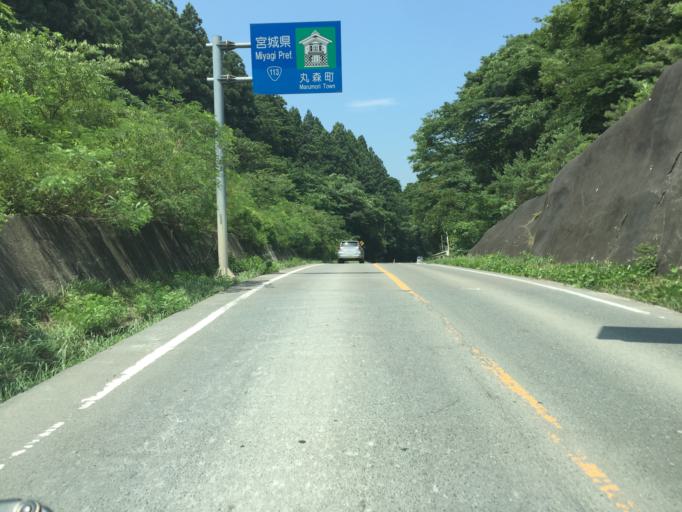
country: JP
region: Miyagi
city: Marumori
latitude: 37.8515
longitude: 140.8533
